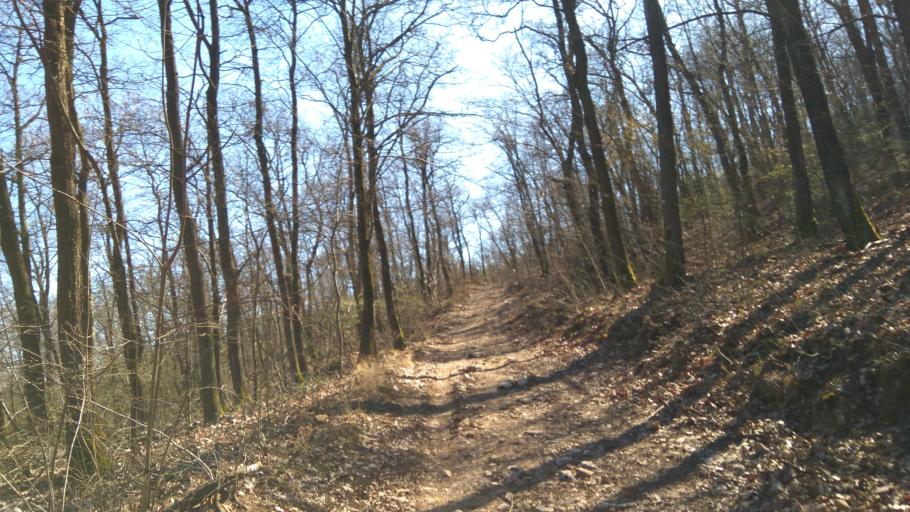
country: HU
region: Pest
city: Csobanka
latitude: 47.6367
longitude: 18.9793
